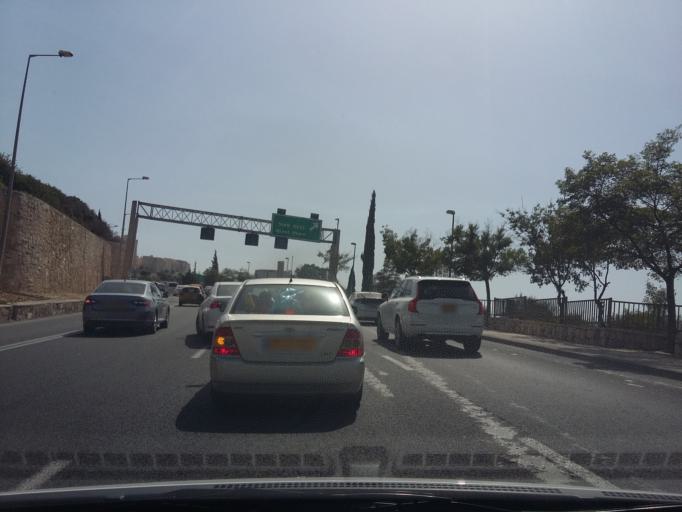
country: IL
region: Jerusalem
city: West Jerusalem
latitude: 31.7992
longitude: 35.2001
